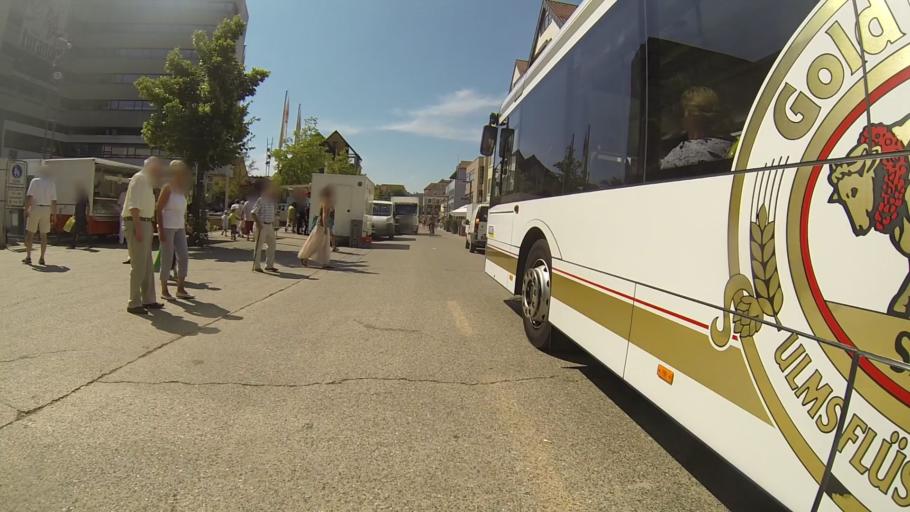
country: DE
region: Baden-Wuerttemberg
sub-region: Regierungsbezirk Stuttgart
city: Heidenheim an der Brenz
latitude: 48.6770
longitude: 10.1526
